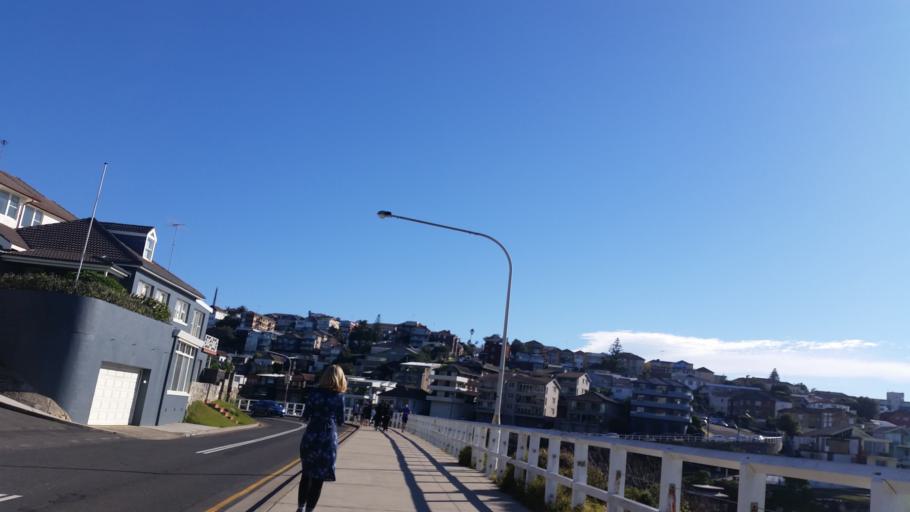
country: AU
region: New South Wales
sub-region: Waverley
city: Bronte
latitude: -33.9012
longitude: 151.2700
